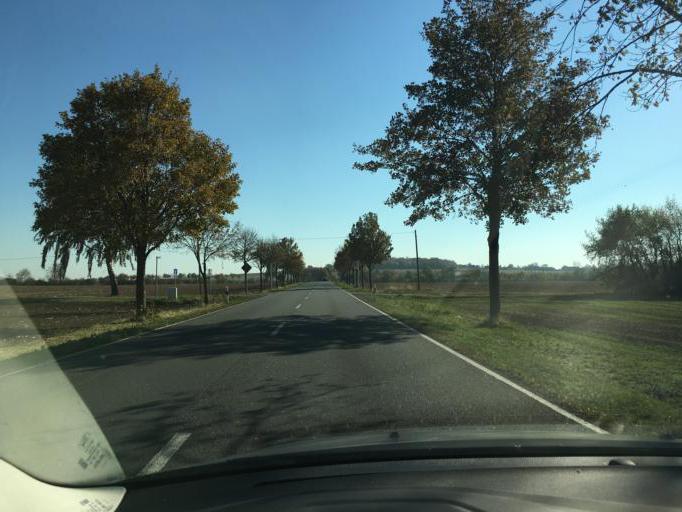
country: DE
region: Saxony-Anhalt
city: Wanzleben
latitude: 52.0409
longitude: 11.4619
